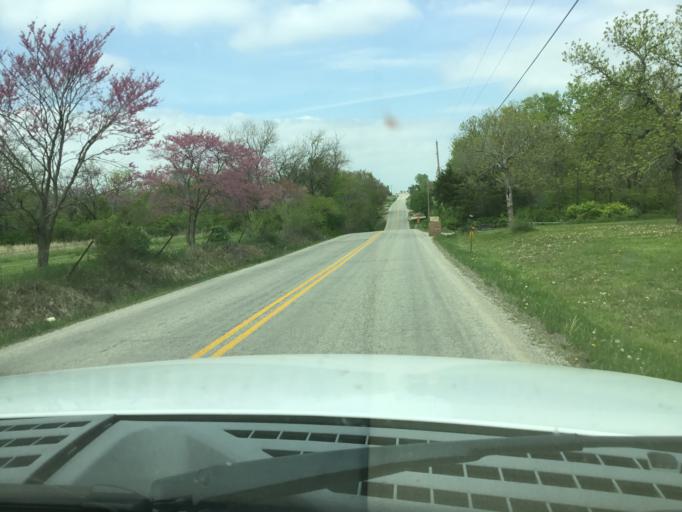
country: US
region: Kansas
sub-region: Shawnee County
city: Topeka
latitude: 38.9797
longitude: -95.6143
